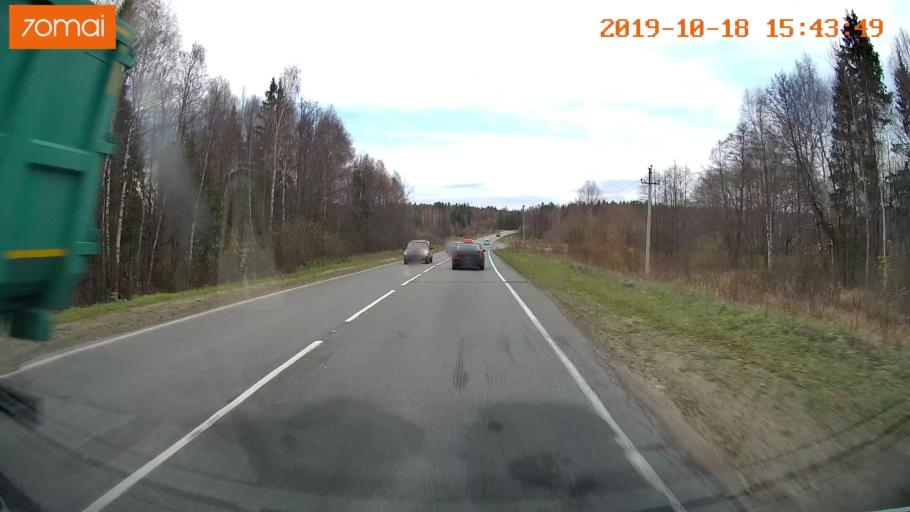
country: RU
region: Vladimir
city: Golovino
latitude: 55.9732
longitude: 40.5476
